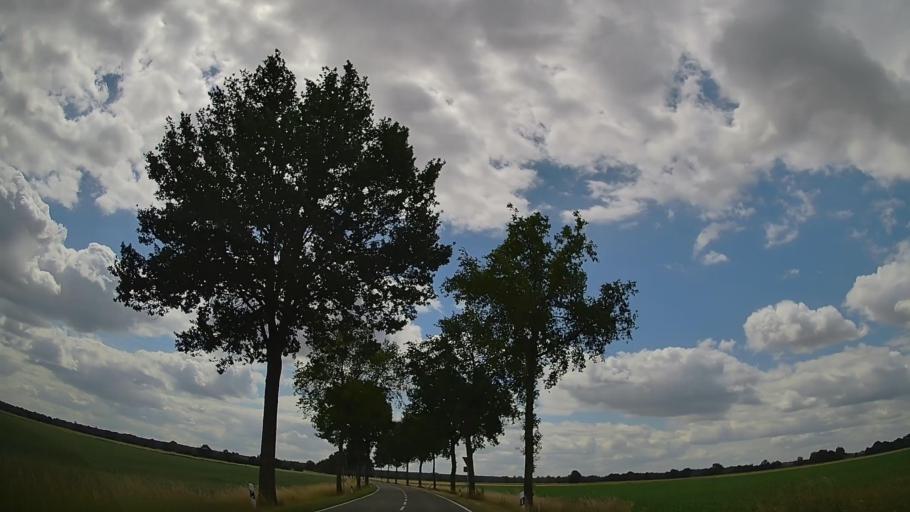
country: DE
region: Lower Saxony
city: Brockum
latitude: 52.4375
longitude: 8.5015
